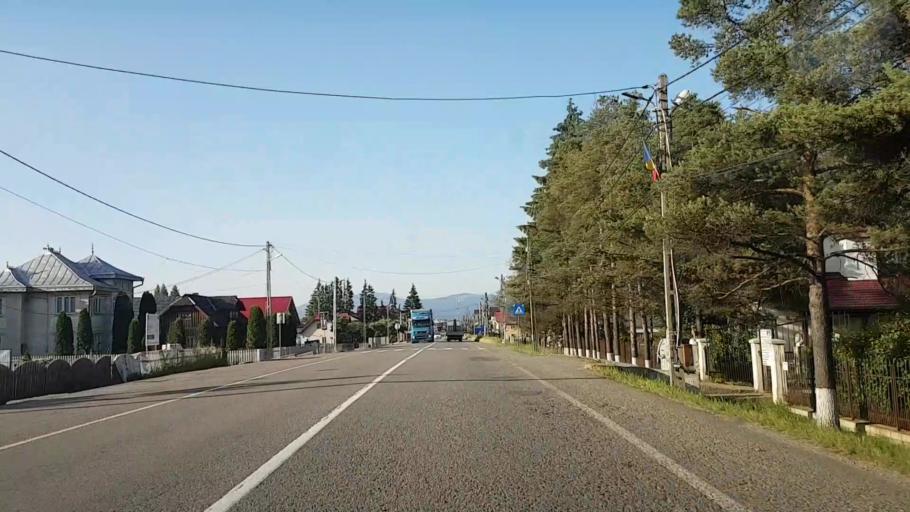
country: RO
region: Suceava
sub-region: Comuna Poiana Stampei
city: Poiana Stampei
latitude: 47.3204
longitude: 25.1368
